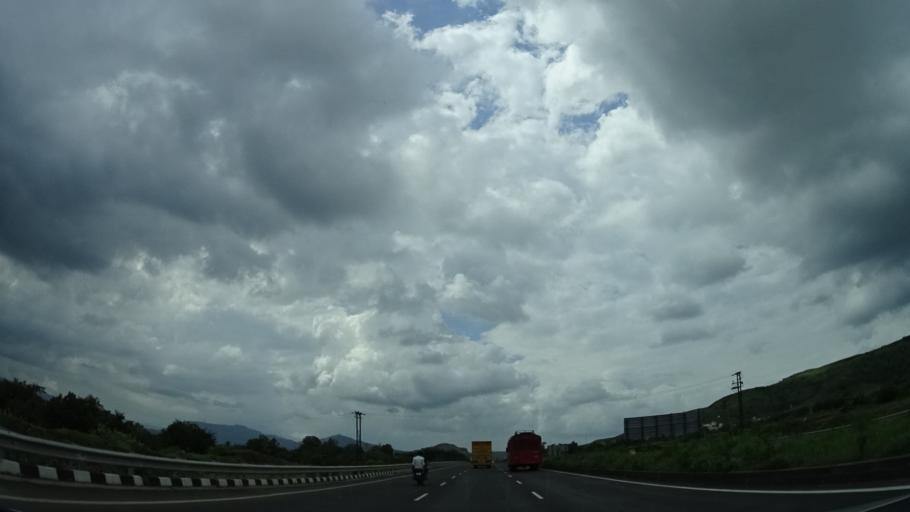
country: IN
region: Maharashtra
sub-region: Satara Division
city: Satara
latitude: 17.7345
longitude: 74.0132
